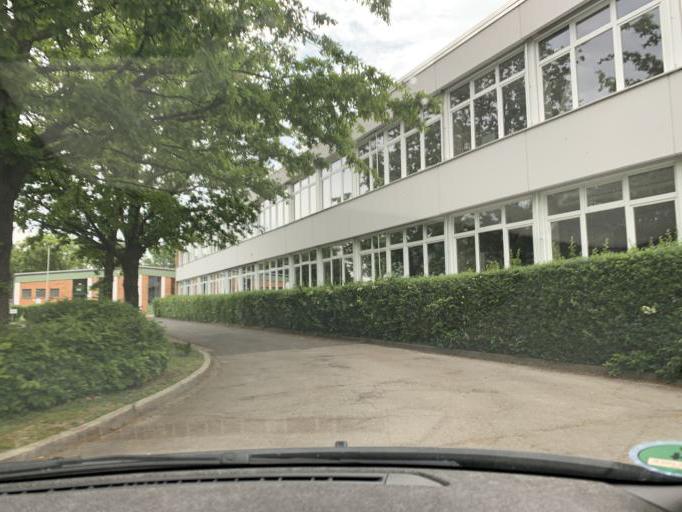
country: DE
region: North Rhine-Westphalia
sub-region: Regierungsbezirk Koln
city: Dueren
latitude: 50.8296
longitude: 6.4648
